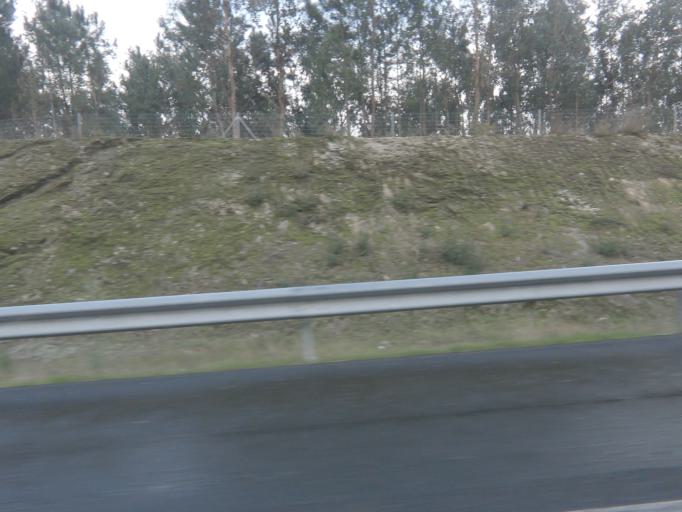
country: ES
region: Galicia
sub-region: Provincia da Coruna
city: Ribeira
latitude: 42.7368
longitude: -8.3674
